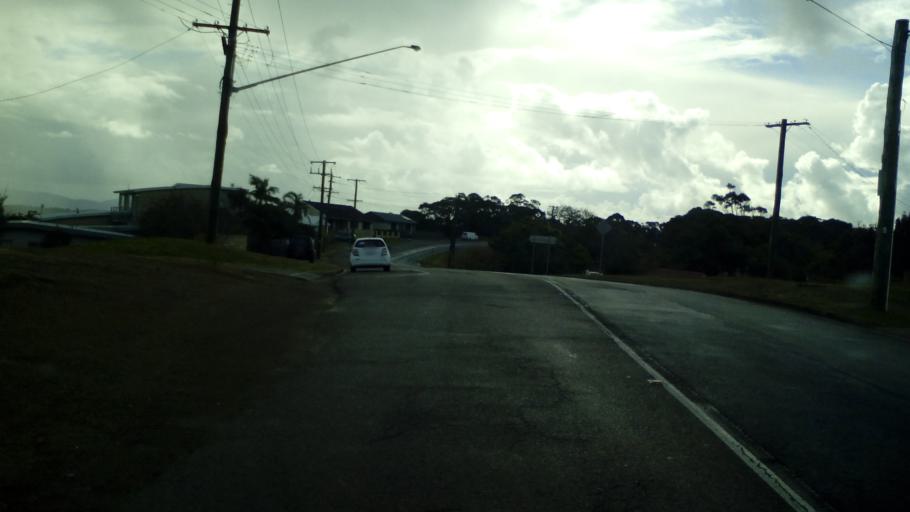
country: AU
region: New South Wales
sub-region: Lake Macquarie Shire
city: Kahibah
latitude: -32.9881
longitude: 151.7150
